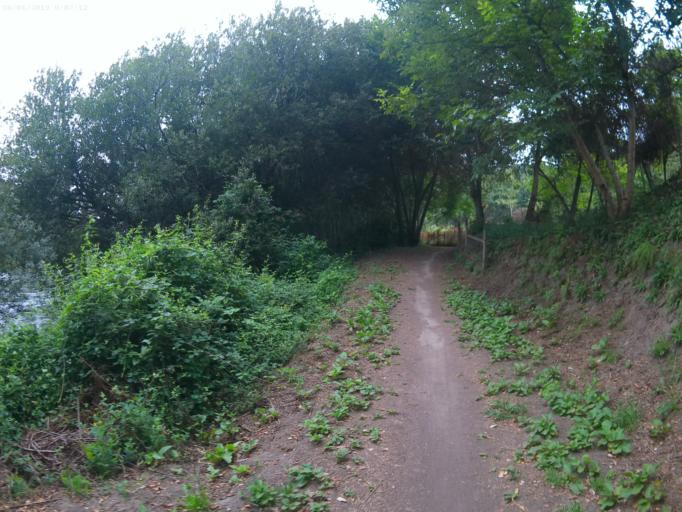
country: PT
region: Viana do Castelo
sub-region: Ponte da Barca
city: Ponte da Barca
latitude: 41.8068
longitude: -8.4468
